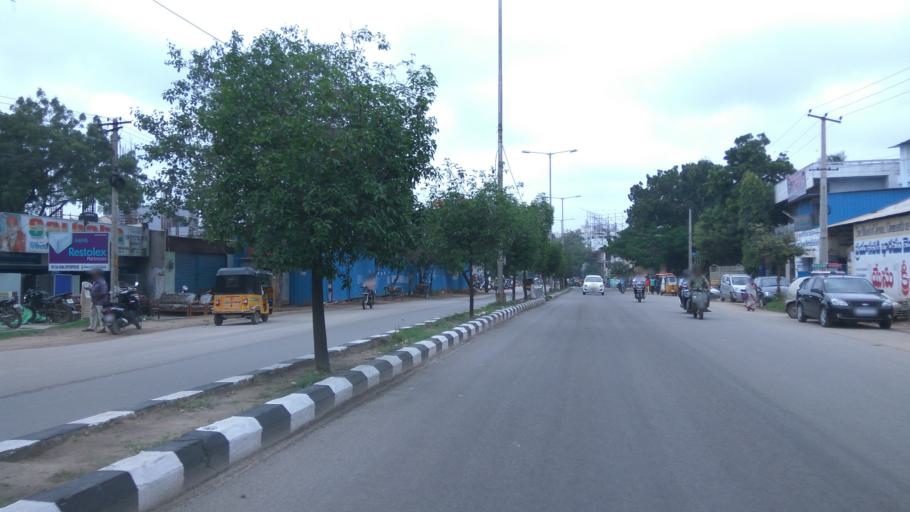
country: IN
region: Telangana
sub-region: Rangareddi
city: Secunderabad
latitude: 17.4814
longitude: 78.5356
